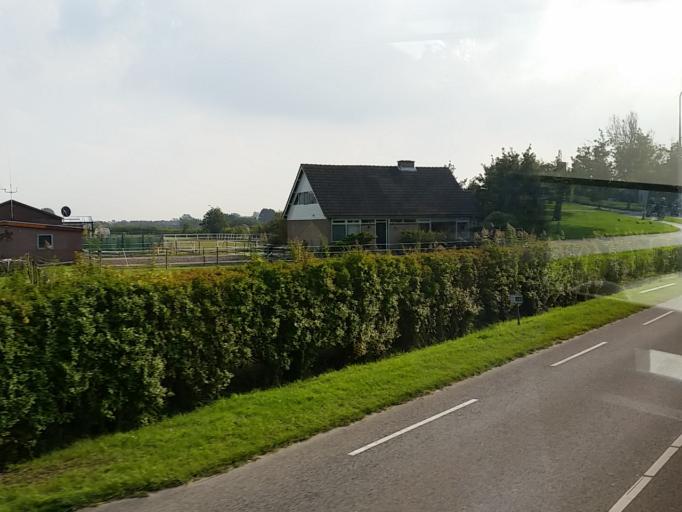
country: NL
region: South Holland
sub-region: Gemeente Noordwijk
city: Noordwijk-Binnen
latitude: 52.2262
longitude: 4.4436
